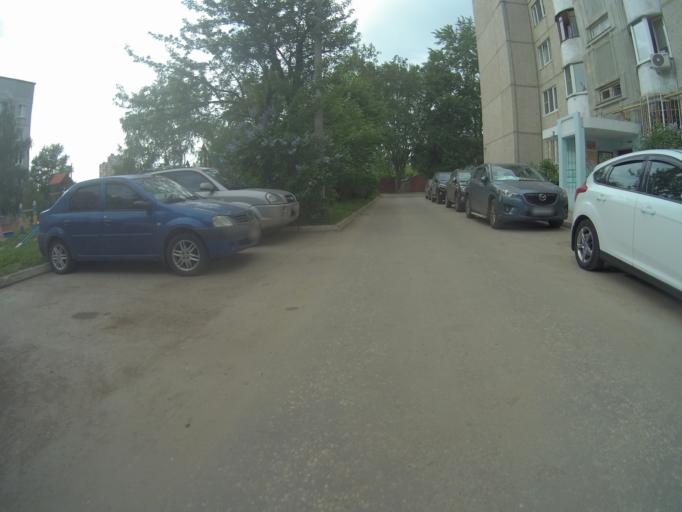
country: RU
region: Vladimir
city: Kommunar
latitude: 56.1630
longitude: 40.4625
